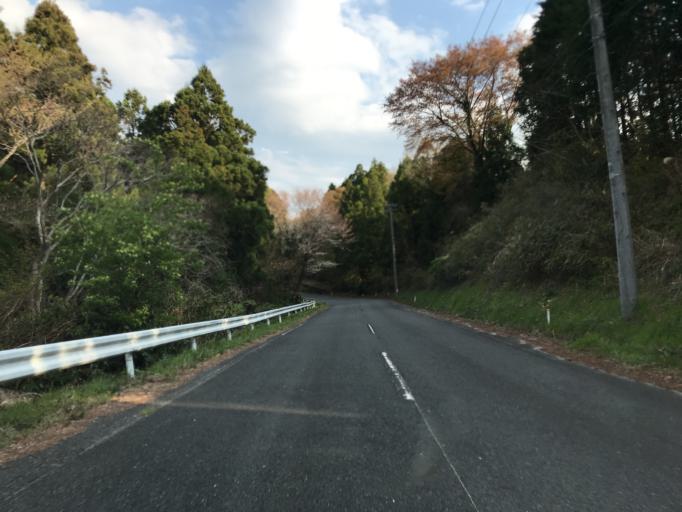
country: JP
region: Fukushima
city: Iwaki
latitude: 37.0809
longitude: 140.9084
